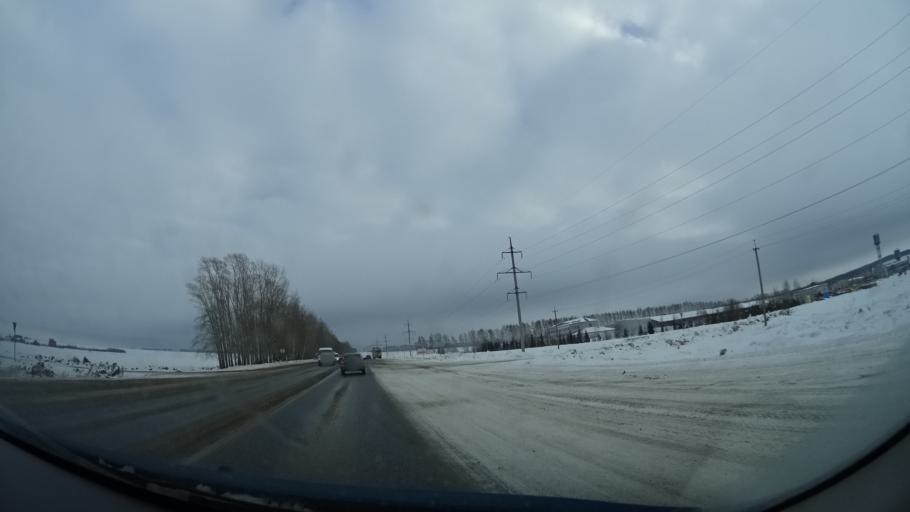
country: RU
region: Bashkortostan
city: Mikhaylovka
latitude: 54.8642
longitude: 55.7499
